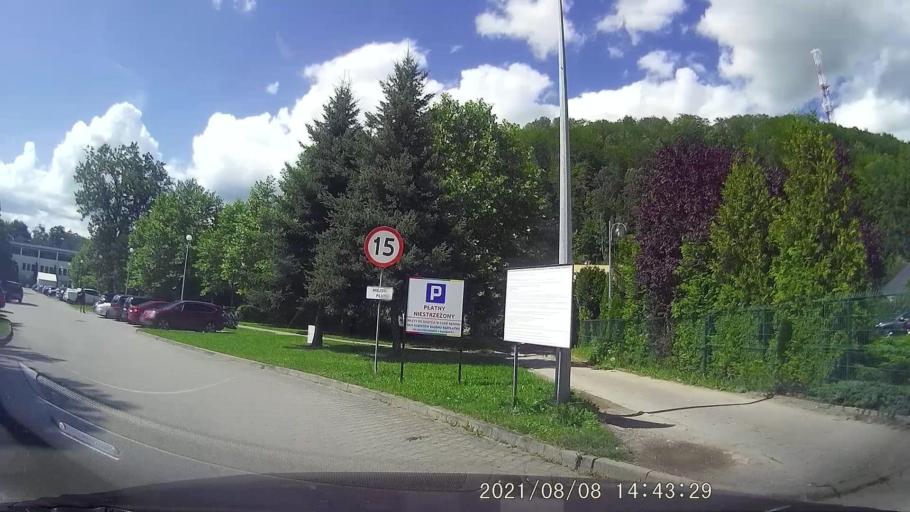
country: PL
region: Lower Silesian Voivodeship
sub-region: Powiat klodzki
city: Kudowa-Zdroj
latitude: 50.4433
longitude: 16.2495
